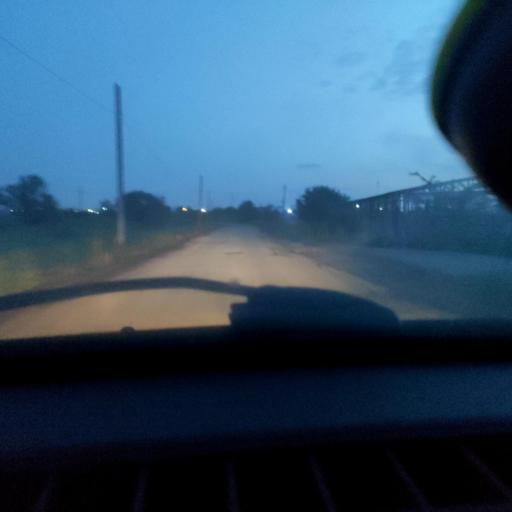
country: RU
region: Samara
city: Tol'yatti
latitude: 53.5698
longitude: 49.3641
